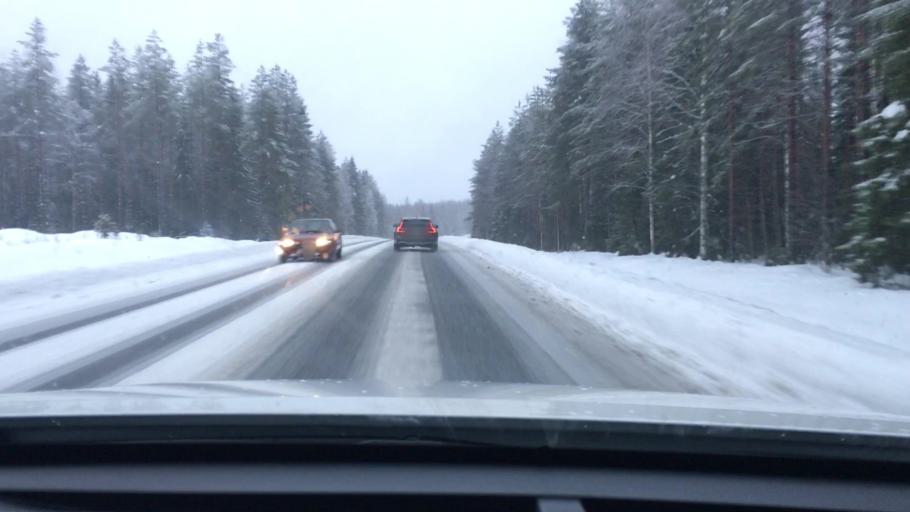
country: FI
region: Northern Savo
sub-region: Ylae-Savo
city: Sonkajaervi
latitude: 63.7722
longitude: 27.4150
